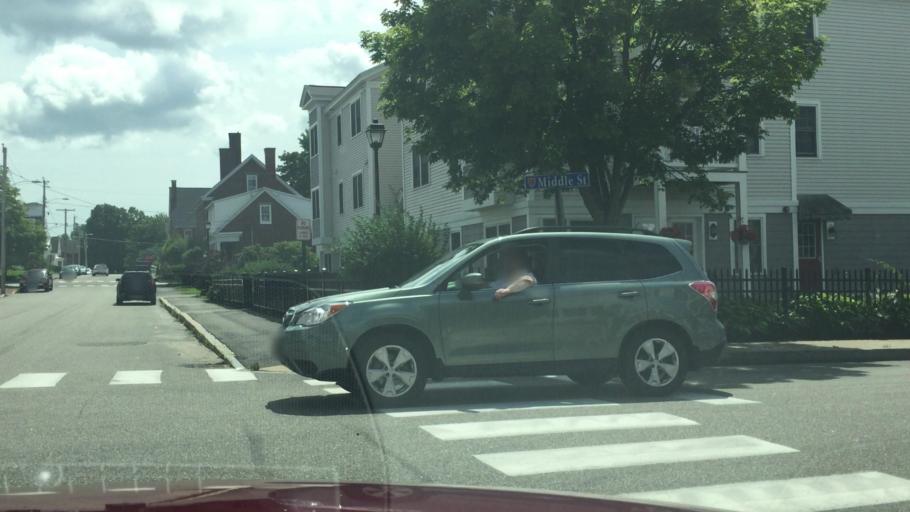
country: US
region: Maine
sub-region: York County
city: Saco
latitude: 43.4983
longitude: -70.4439
